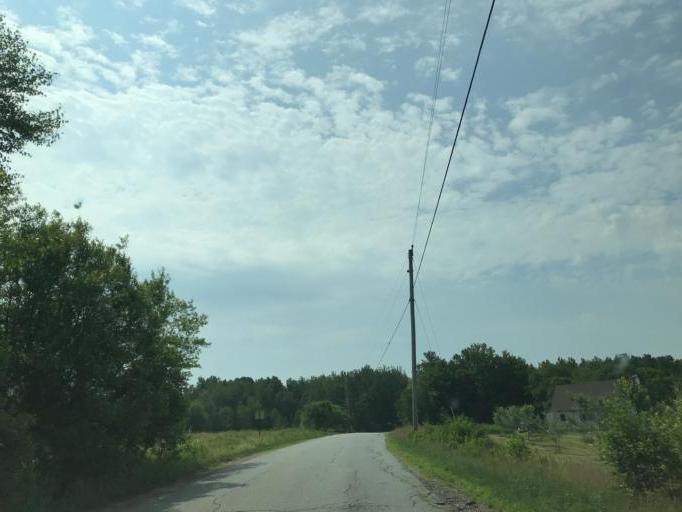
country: US
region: Maine
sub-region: Knox County
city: Hope
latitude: 44.2196
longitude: -69.1722
